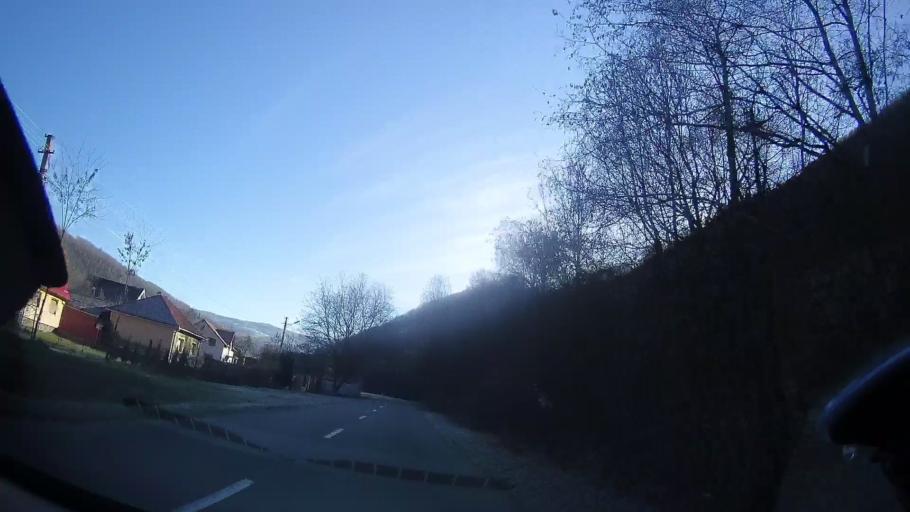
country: RO
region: Bihor
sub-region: Comuna Bulz
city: Bulz
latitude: 46.9089
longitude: 22.6791
